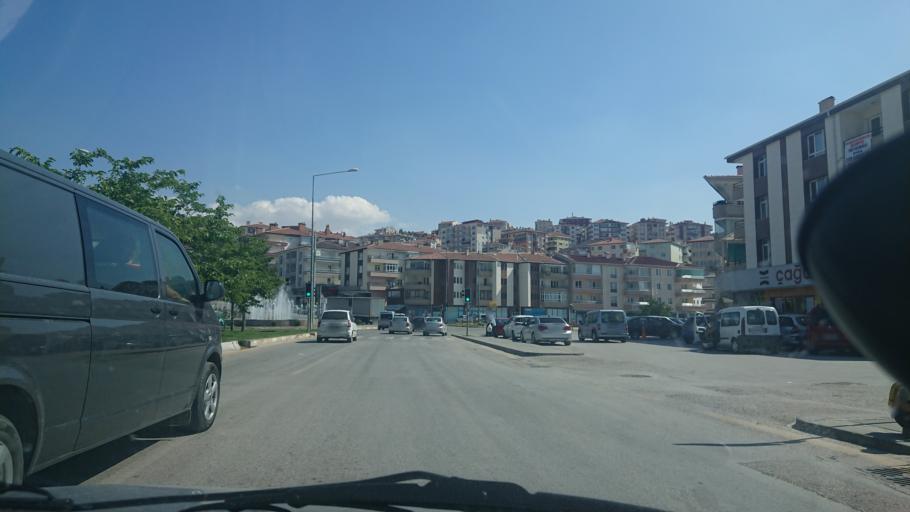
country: TR
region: Ankara
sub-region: Goelbasi
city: Golbasi
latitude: 39.8004
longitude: 32.8115
